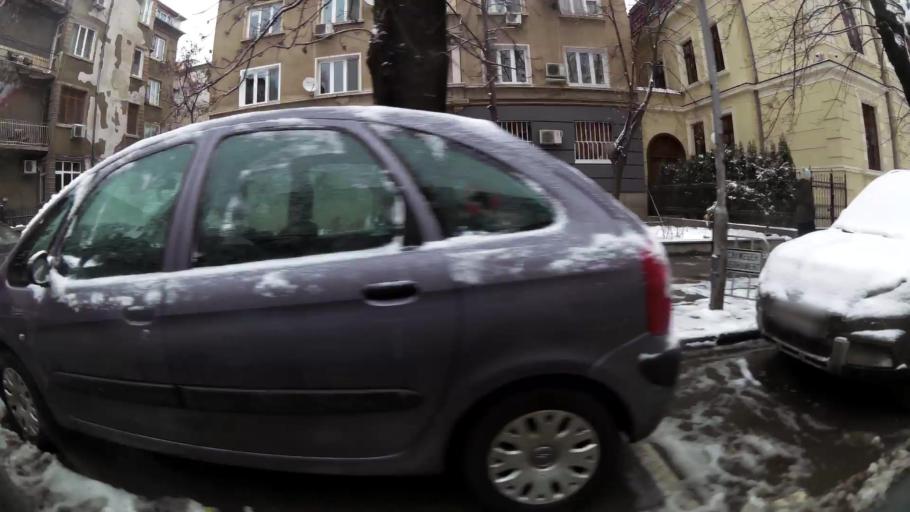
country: BG
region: Sofia-Capital
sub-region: Stolichna Obshtina
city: Sofia
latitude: 42.6946
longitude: 23.3427
